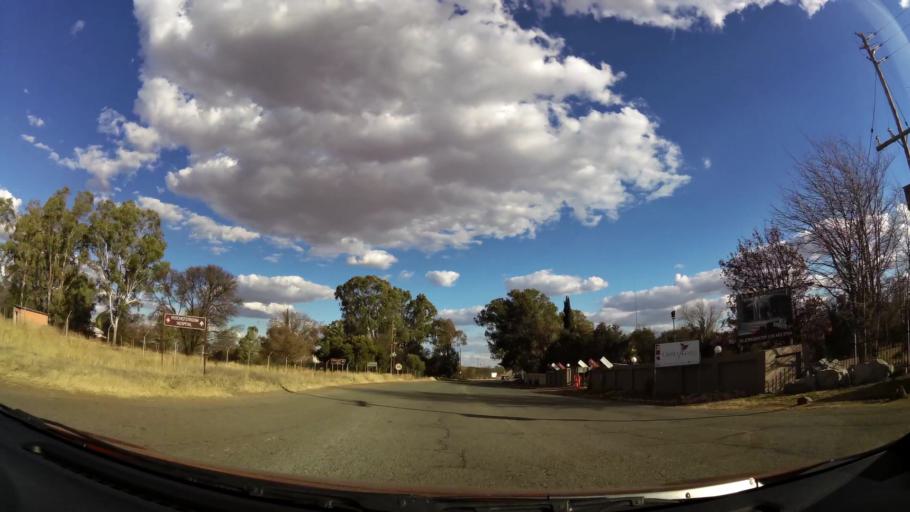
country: ZA
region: North-West
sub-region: Dr Kenneth Kaunda District Municipality
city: Potchefstroom
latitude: -26.6727
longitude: 27.1061
